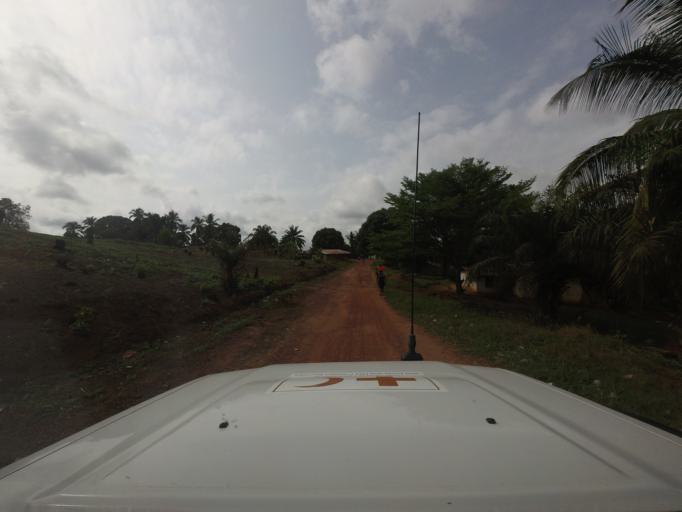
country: LR
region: Bong
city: Gbarnga
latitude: 7.0051
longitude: -9.4744
